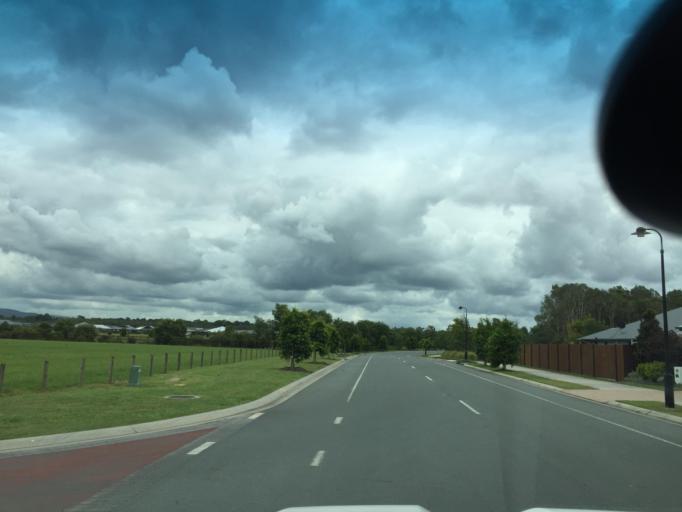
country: AU
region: Queensland
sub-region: Moreton Bay
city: Caboolture
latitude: -27.0645
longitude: 152.9303
